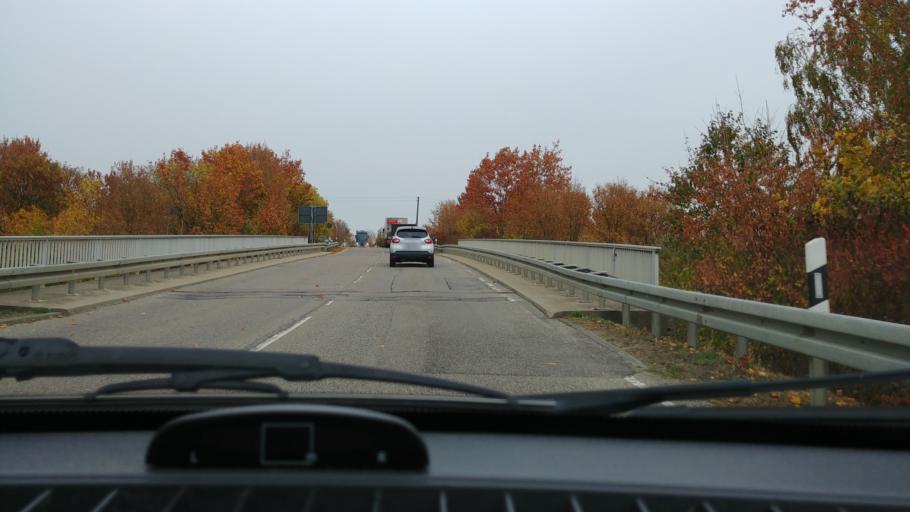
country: DE
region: Baden-Wuerttemberg
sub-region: Regierungsbezirk Stuttgart
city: Rot am See
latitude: 49.2467
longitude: 10.0307
